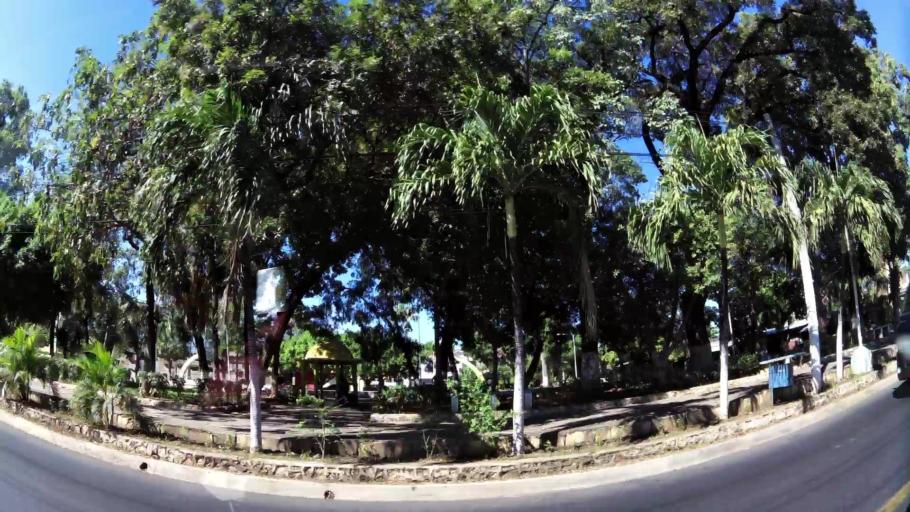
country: SV
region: San Miguel
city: San Miguel
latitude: 13.4744
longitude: -88.1715
